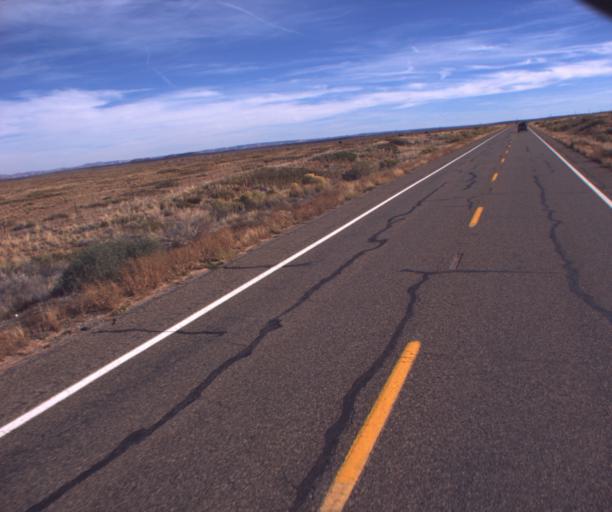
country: US
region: Arizona
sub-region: Coconino County
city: Kaibito
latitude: 36.6156
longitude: -110.9877
